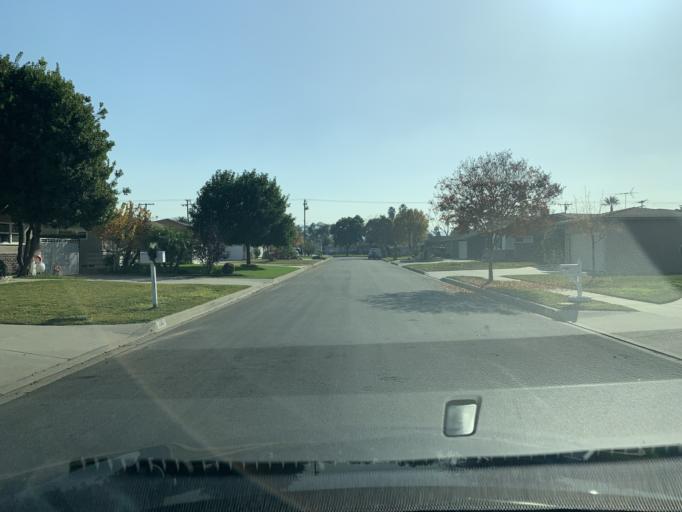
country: US
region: California
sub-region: Los Angeles County
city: Covina
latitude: 34.0766
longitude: -117.8980
